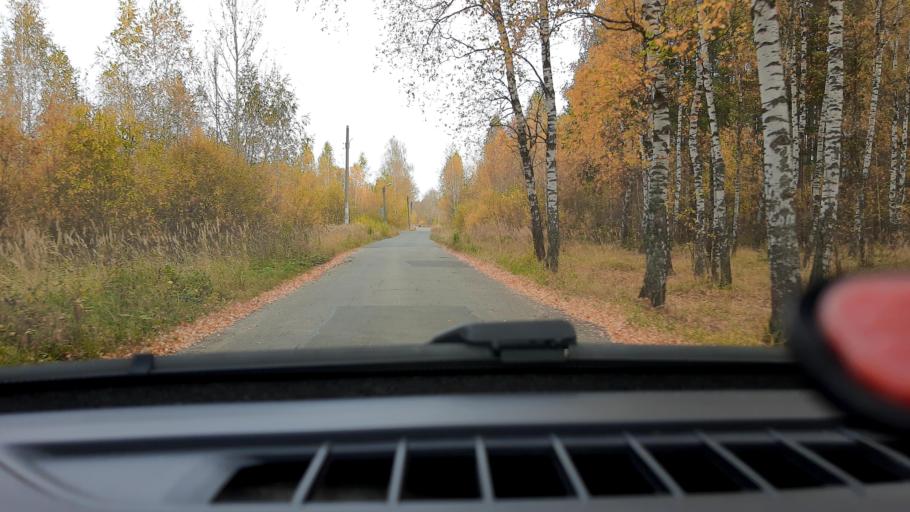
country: RU
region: Nizjnij Novgorod
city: Gorbatovka
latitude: 56.2898
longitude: 43.8311
